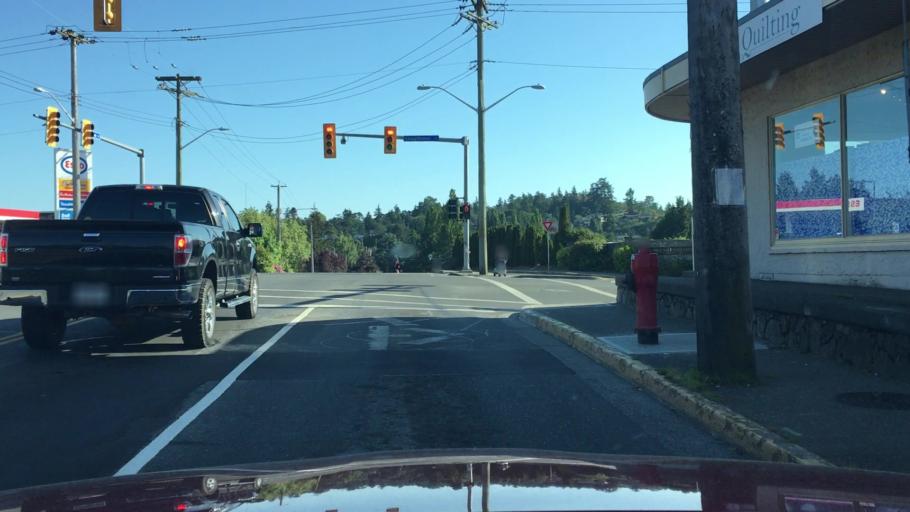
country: CA
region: British Columbia
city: Victoria
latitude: 48.4422
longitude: -123.4022
